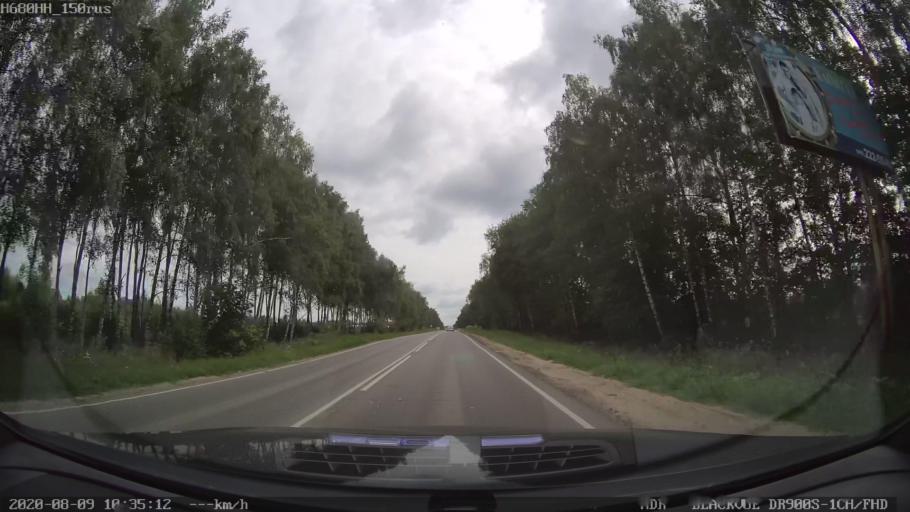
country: RU
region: Tula
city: Zaokskiy
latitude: 54.7380
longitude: 37.3625
